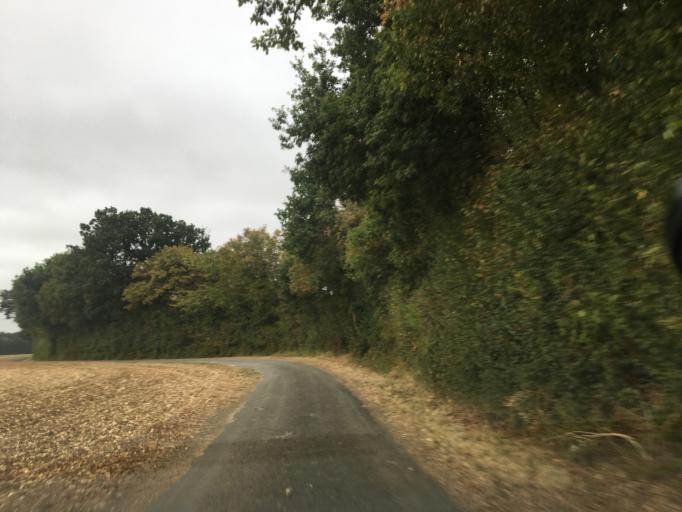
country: FR
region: Poitou-Charentes
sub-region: Departement des Deux-Sevres
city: Beauvoir-sur-Niort
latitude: 46.0846
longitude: -0.5249
